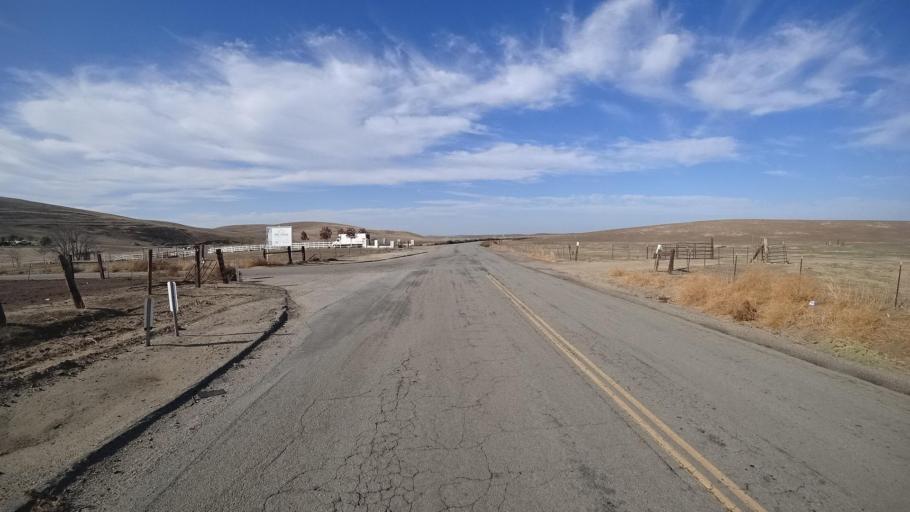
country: US
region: California
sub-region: Tulare County
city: Richgrove
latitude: 35.6205
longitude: -119.0225
